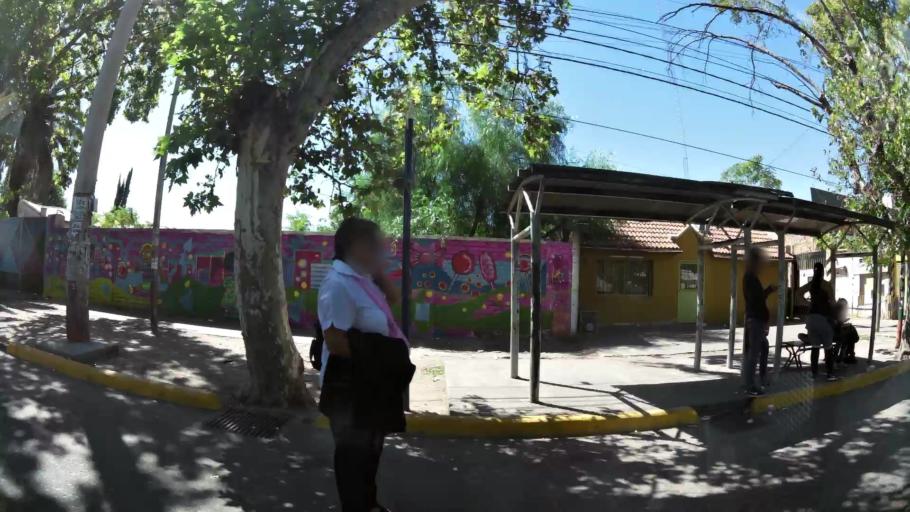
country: AR
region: Mendoza
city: Villa Nueva
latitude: -32.8971
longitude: -68.8038
